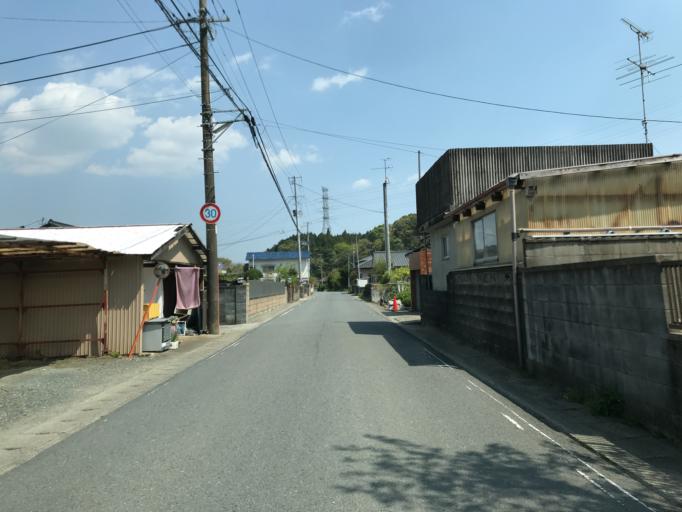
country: JP
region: Ibaraki
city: Kitaibaraki
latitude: 36.9180
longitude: 140.7491
